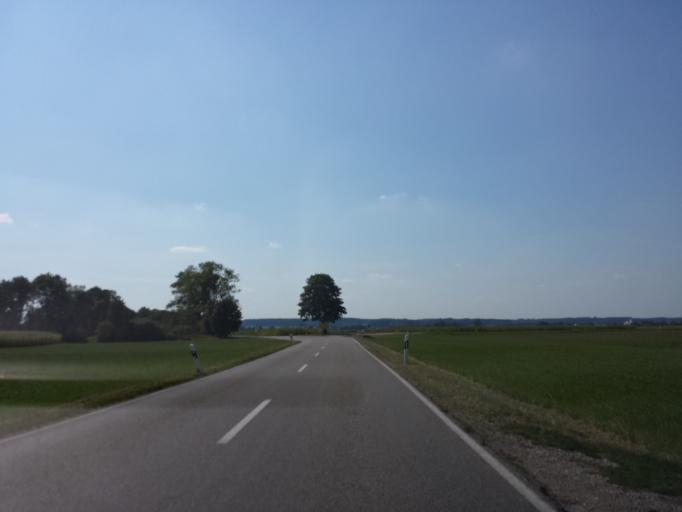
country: DE
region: Bavaria
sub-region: Swabia
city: Turkheim
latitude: 48.0624
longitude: 10.6096
